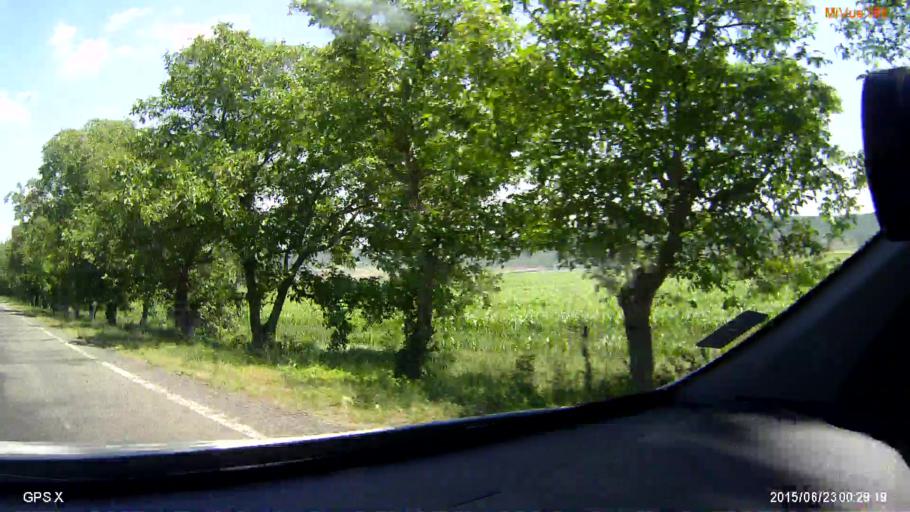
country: RO
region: Iasi
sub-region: Comuna Grozesti
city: Grozesti
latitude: 47.0366
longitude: 28.0838
